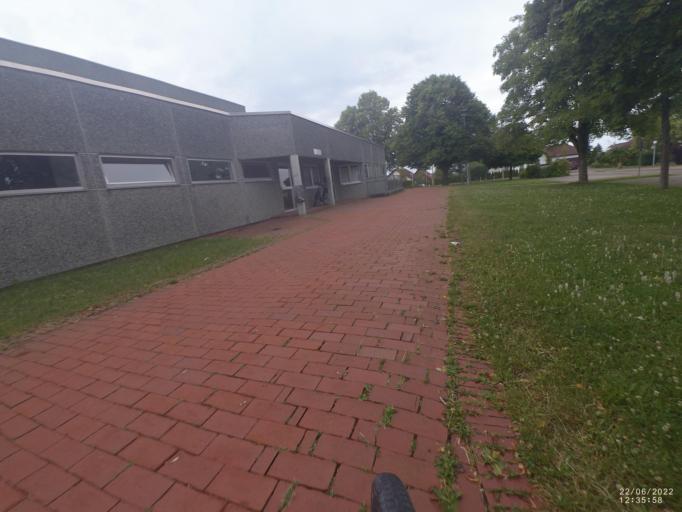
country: DE
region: Baden-Wuerttemberg
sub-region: Regierungsbezirk Stuttgart
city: Gerstetten
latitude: 48.6184
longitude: 10.0193
